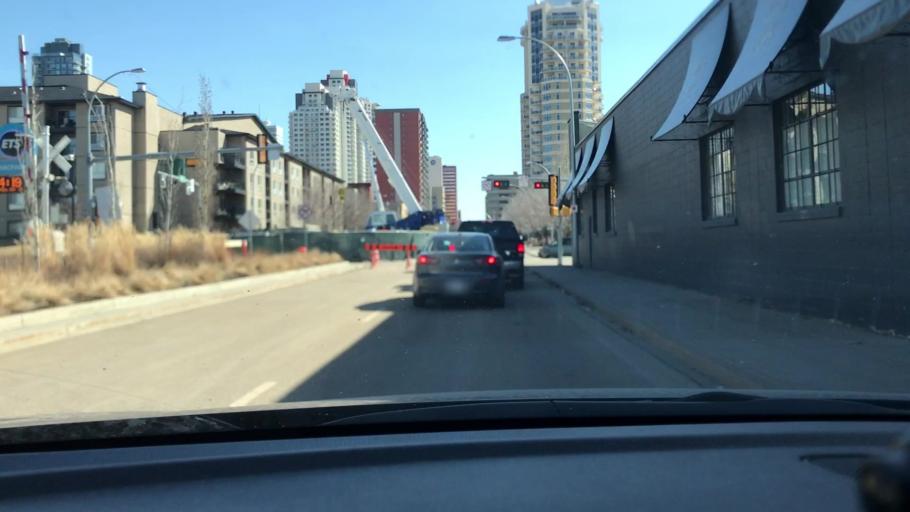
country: CA
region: Alberta
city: Edmonton
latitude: 53.5483
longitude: -113.5012
